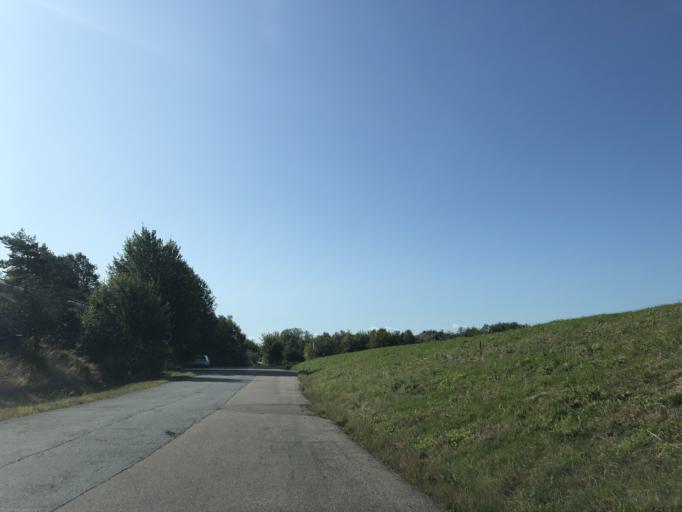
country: SE
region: Vaestra Goetaland
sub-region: Goteborg
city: Torslanda
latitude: 57.7136
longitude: 11.8060
